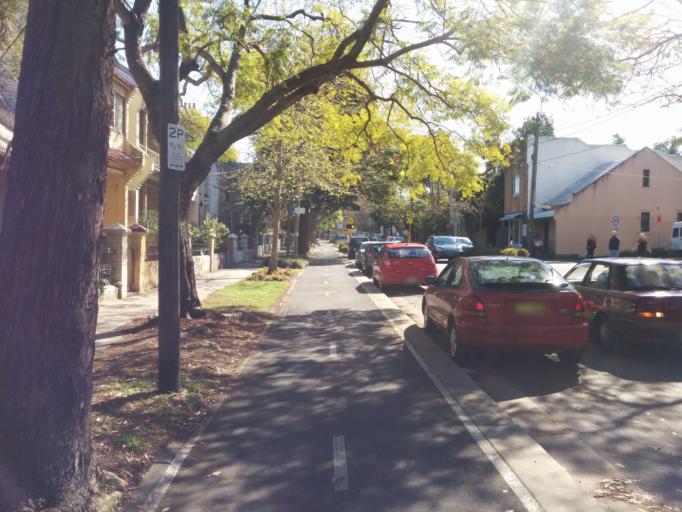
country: AU
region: New South Wales
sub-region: City of Sydney
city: Redfern
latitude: -33.8953
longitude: 151.2135
